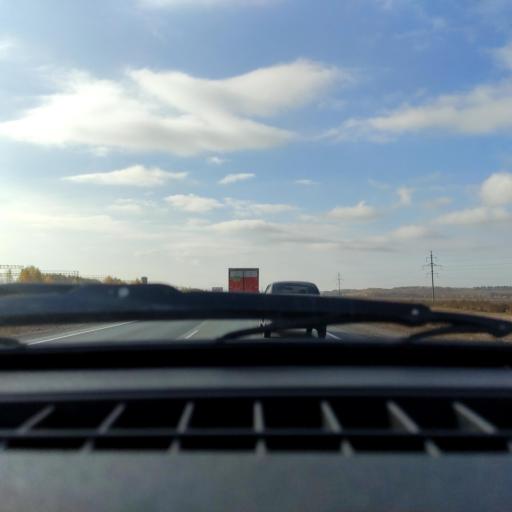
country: RU
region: Bashkortostan
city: Kabakovo
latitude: 54.7105
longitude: 56.2266
